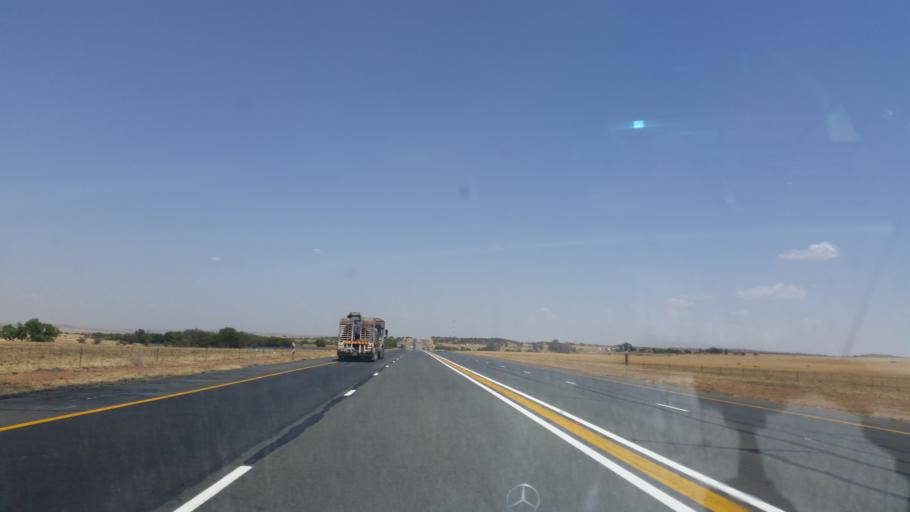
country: ZA
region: Orange Free State
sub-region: Lejweleputswa District Municipality
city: Brandfort
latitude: -28.8964
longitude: 26.4753
